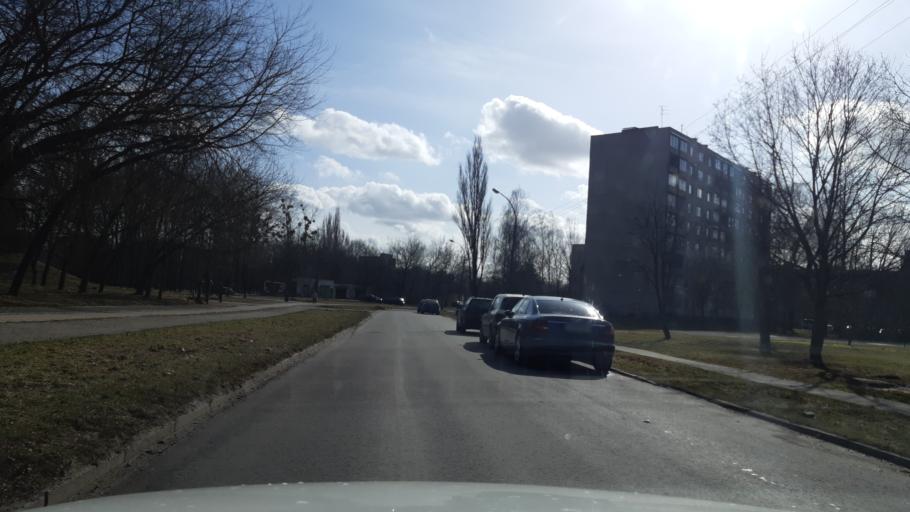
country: LT
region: Kauno apskritis
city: Dainava (Kaunas)
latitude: 54.9157
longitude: 23.9681
